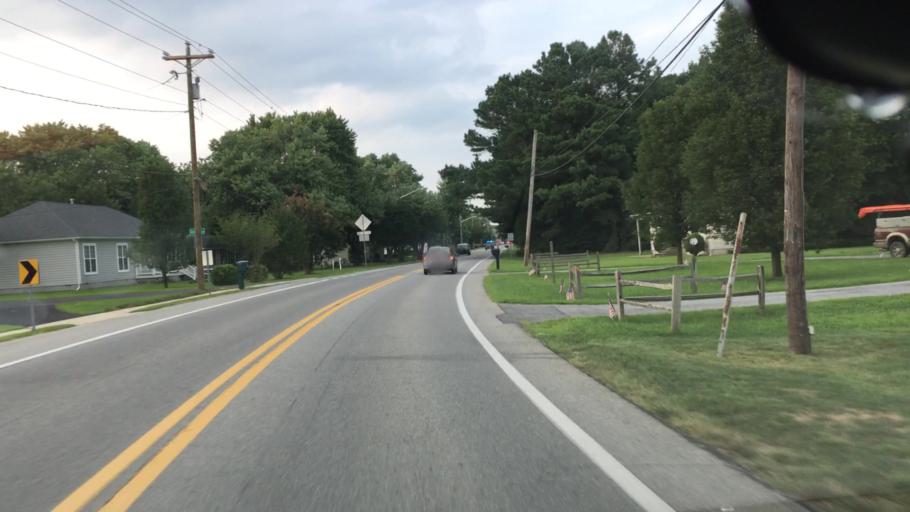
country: US
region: Delaware
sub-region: Sussex County
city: Ocean View
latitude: 38.5379
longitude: -75.0913
